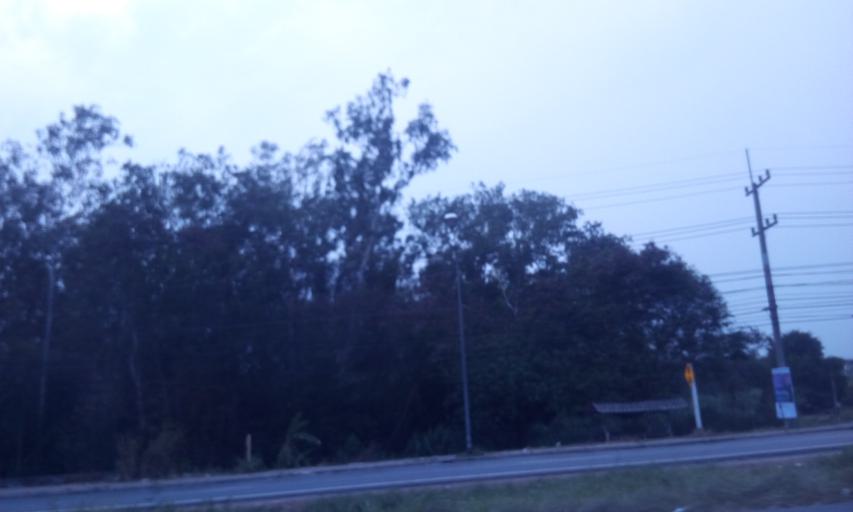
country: TH
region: Chon Buri
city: Ban Bueng
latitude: 13.2813
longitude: 101.2552
